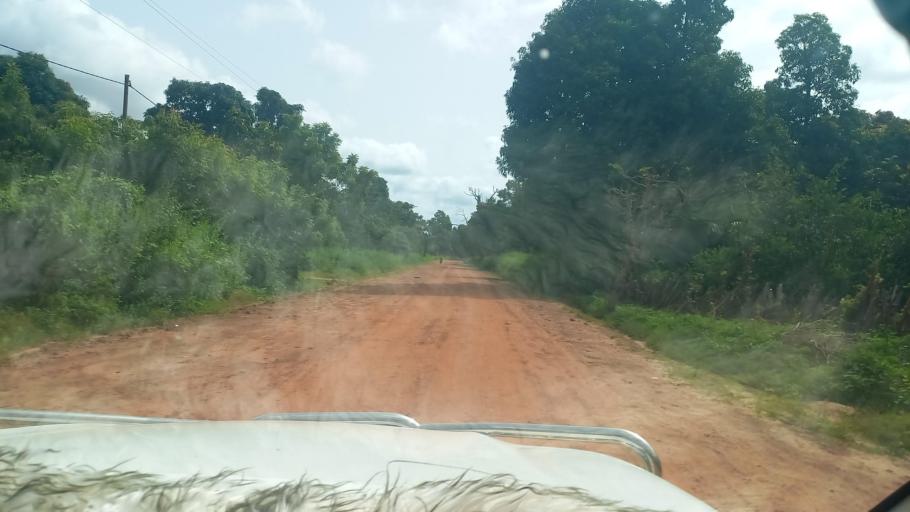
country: SN
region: Ziguinchor
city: Bignona
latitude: 12.7514
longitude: -16.2793
